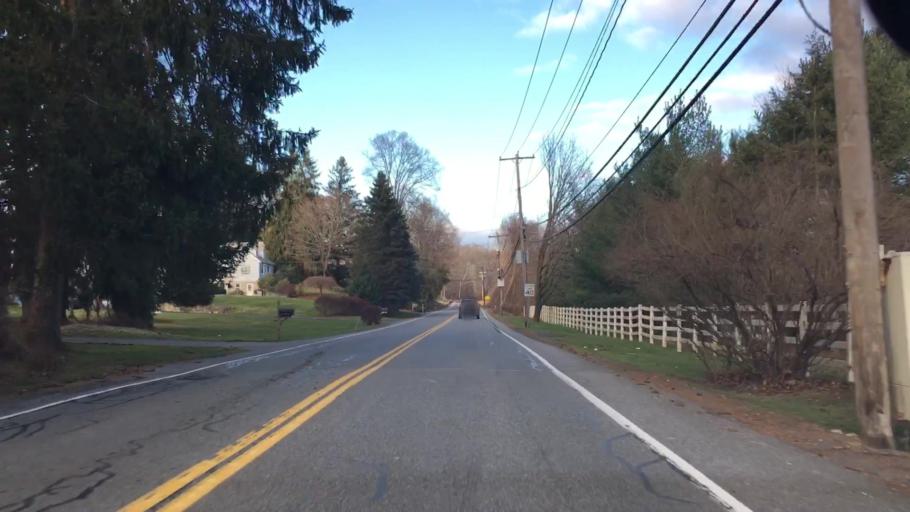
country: US
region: New York
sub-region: Putnam County
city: Carmel
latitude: 41.4367
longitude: -73.6524
